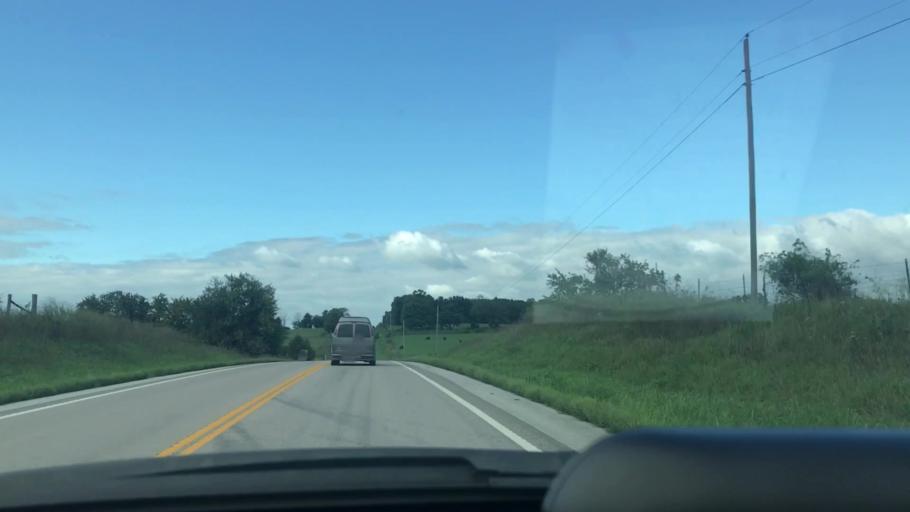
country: US
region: Missouri
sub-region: Hickory County
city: Hermitage
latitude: 37.9592
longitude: -93.2070
